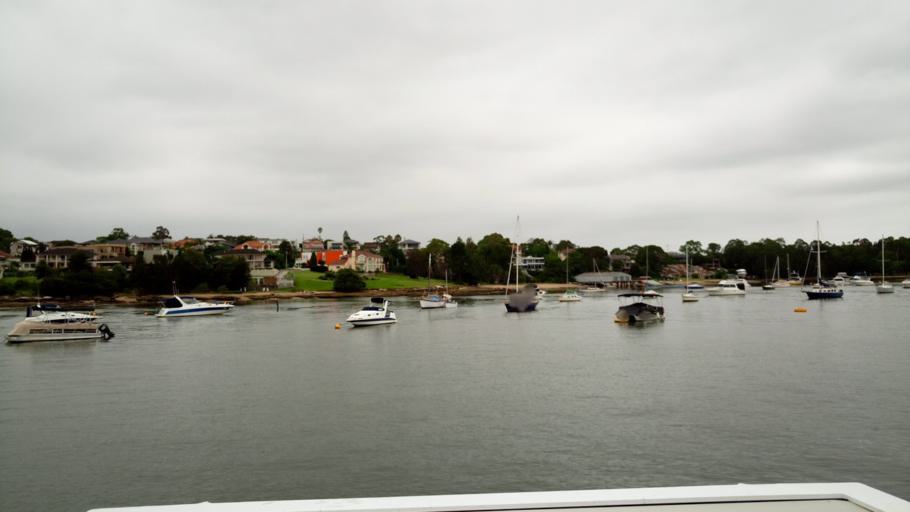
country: AU
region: New South Wales
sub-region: Canada Bay
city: Concord
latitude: -33.8324
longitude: 151.1031
